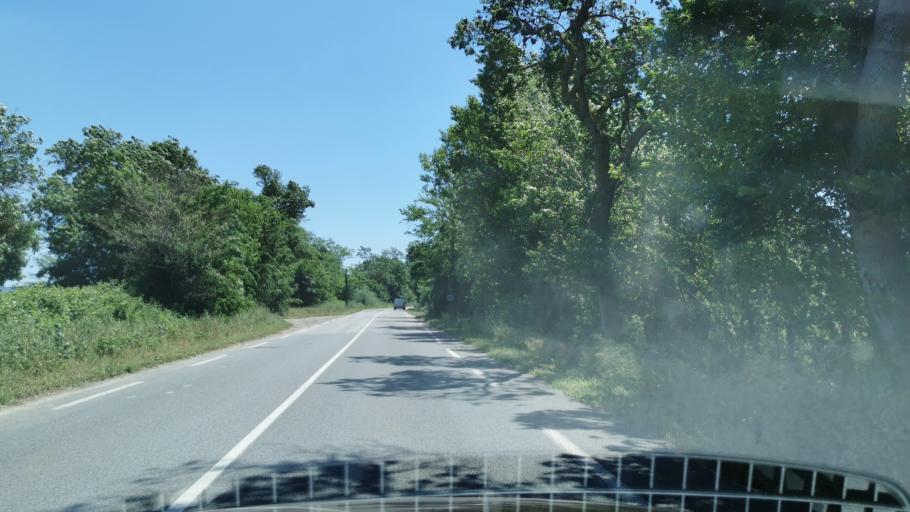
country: FR
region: Languedoc-Roussillon
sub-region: Departement de l'Aude
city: Narbonne
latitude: 43.2133
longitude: 3.0120
